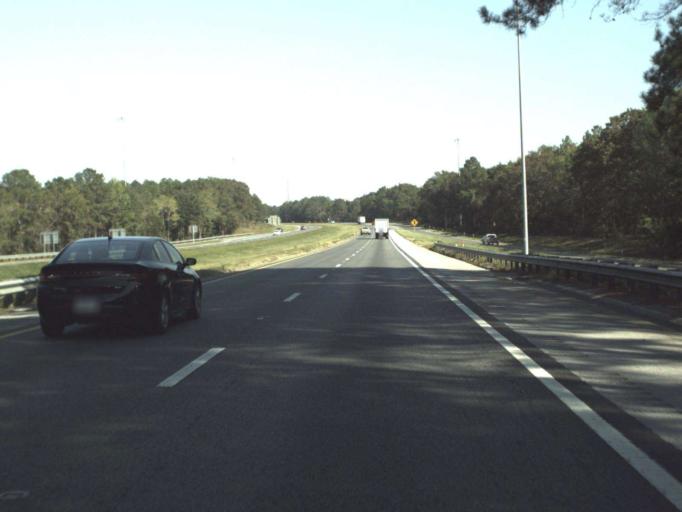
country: US
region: Florida
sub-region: Washington County
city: Chipley
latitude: 30.7476
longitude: -85.5505
